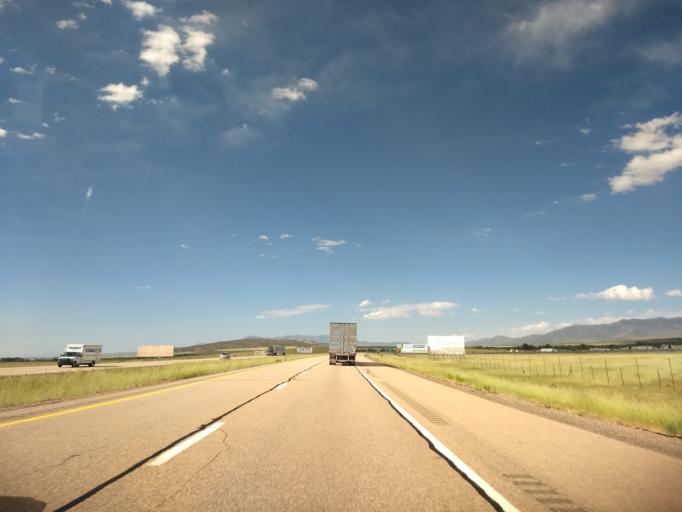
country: US
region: Utah
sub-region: Millard County
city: Fillmore
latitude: 38.9732
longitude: -112.3412
